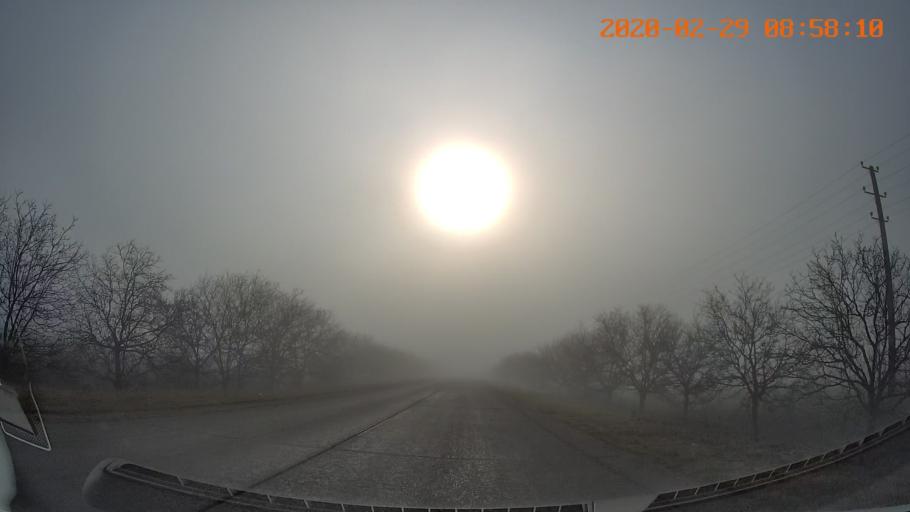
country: MD
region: Telenesti
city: Tiraspolul Nou
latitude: 46.9228
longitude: 29.6371
